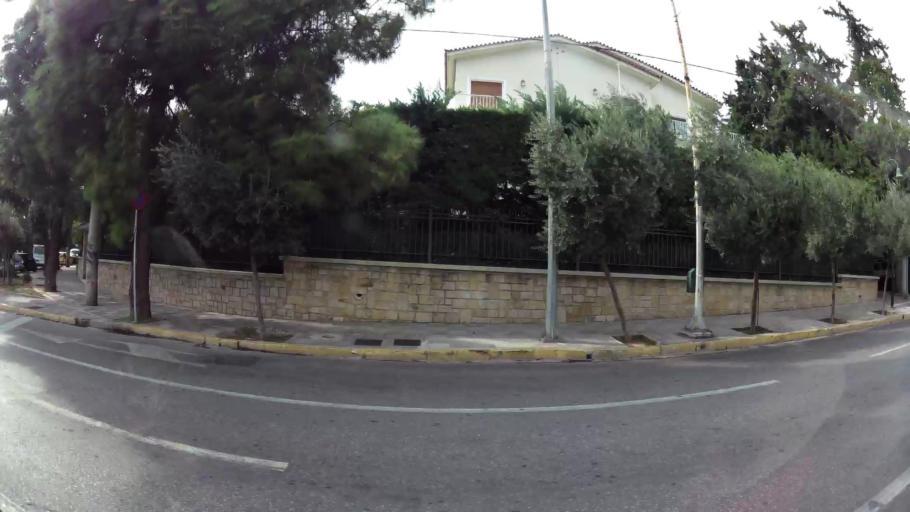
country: GR
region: Attica
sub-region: Nomarchia Athinas
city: Neo Psychiko
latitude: 38.0051
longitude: 23.7754
